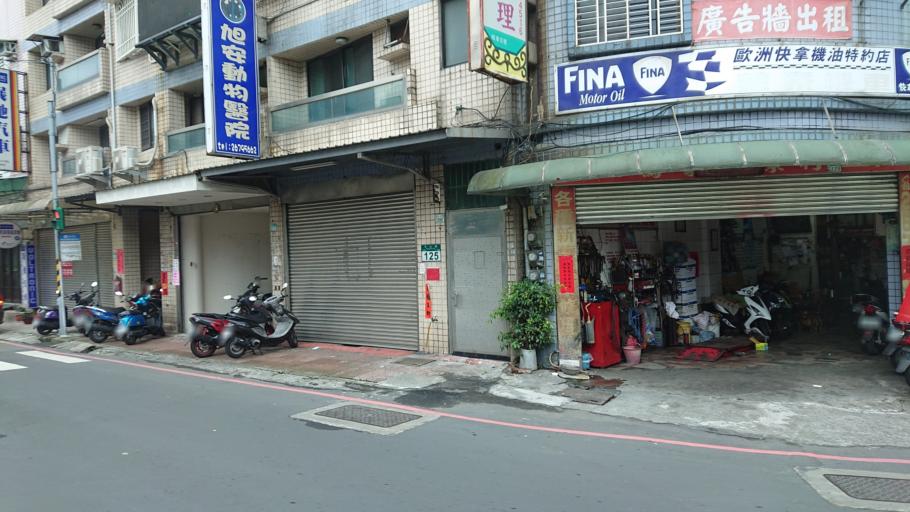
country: TW
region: Taiwan
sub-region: Taoyuan
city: Taoyuan
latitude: 24.9570
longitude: 121.3497
